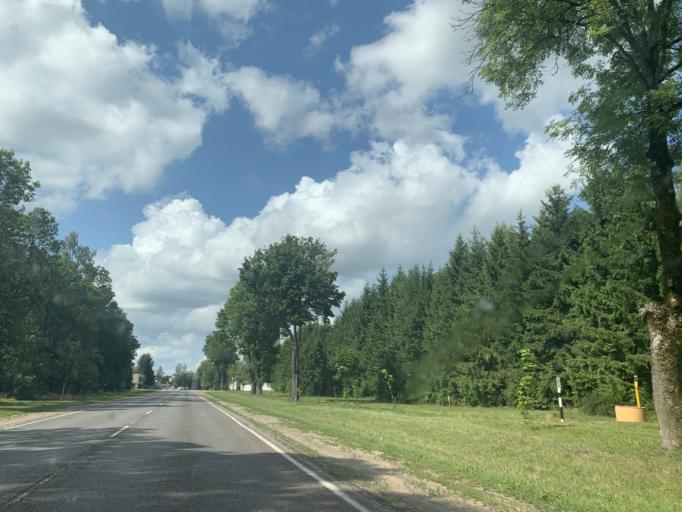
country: BY
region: Minsk
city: Enyerhyetykaw
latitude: 53.5820
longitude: 27.0548
